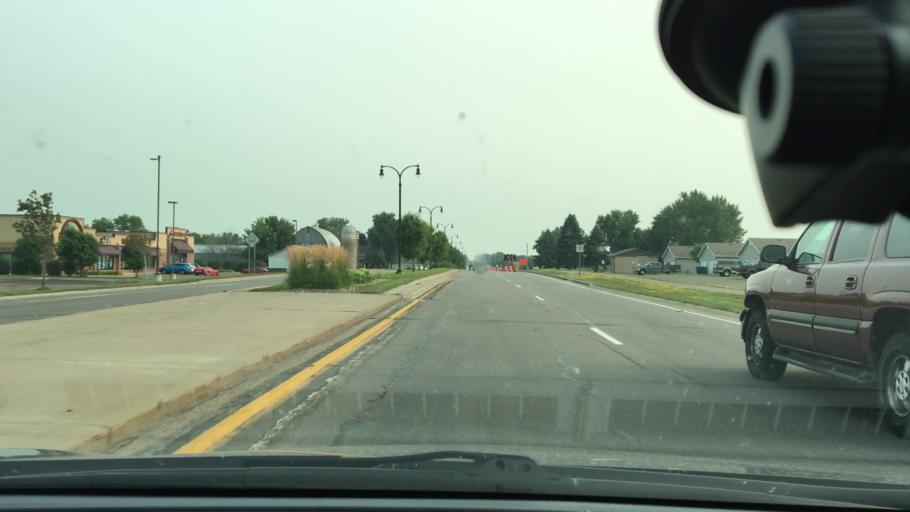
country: US
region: Minnesota
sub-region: Wright County
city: Albertville
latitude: 45.2334
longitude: -93.6644
